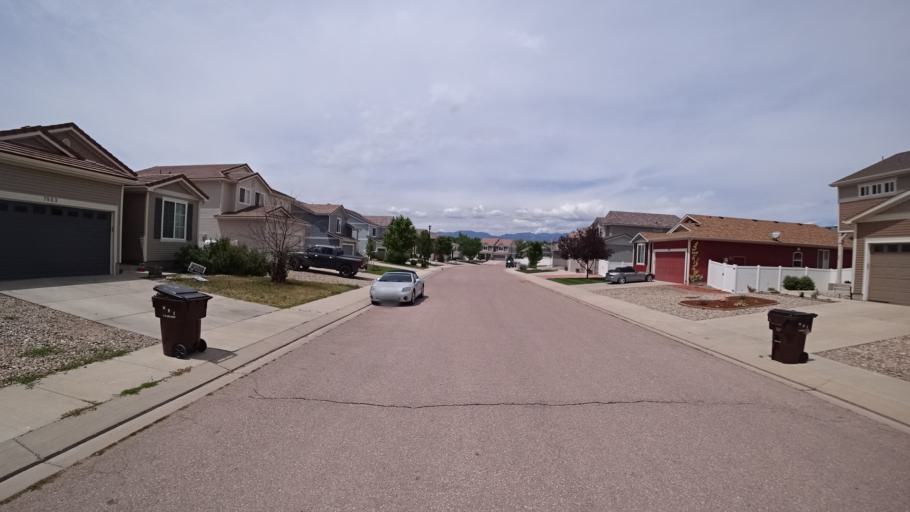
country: US
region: Colorado
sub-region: El Paso County
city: Fountain
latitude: 38.6950
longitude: -104.6804
